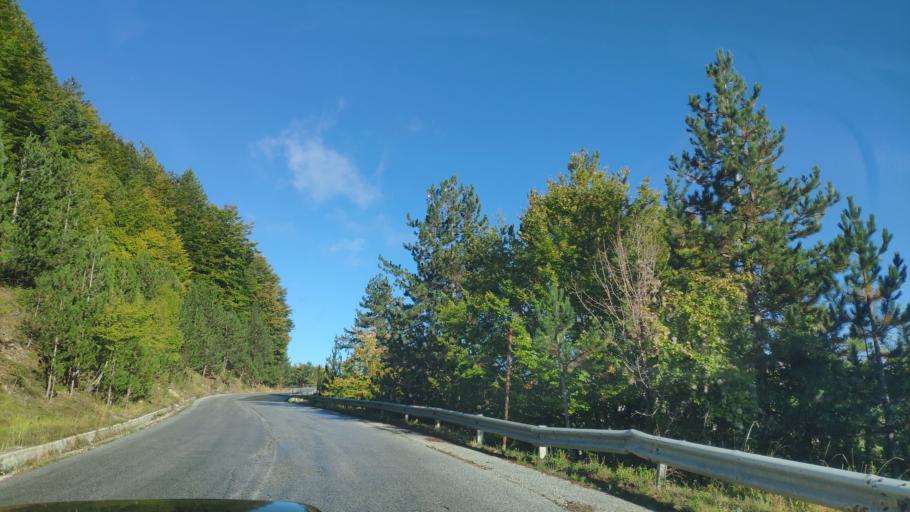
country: GR
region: Epirus
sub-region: Nomos Ioanninon
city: Metsovo
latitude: 39.7761
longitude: 21.1760
